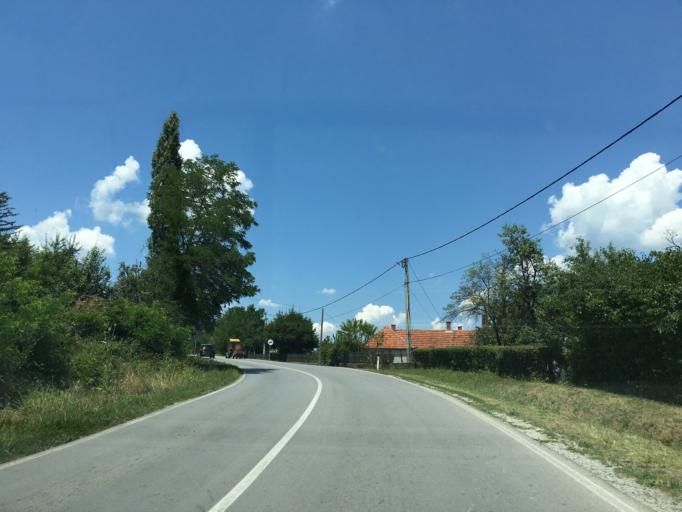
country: RS
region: Central Serbia
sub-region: Kolubarski Okrug
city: Ljig
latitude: 44.2321
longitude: 20.2321
